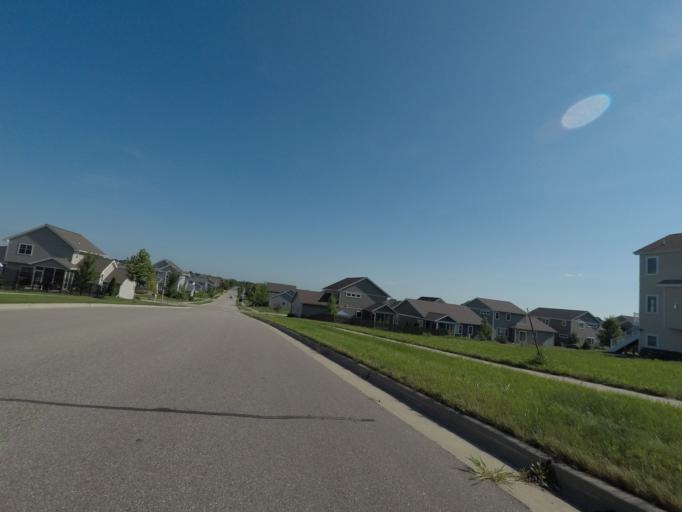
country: US
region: Wisconsin
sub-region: Dane County
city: Middleton
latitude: 43.0641
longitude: -89.5488
